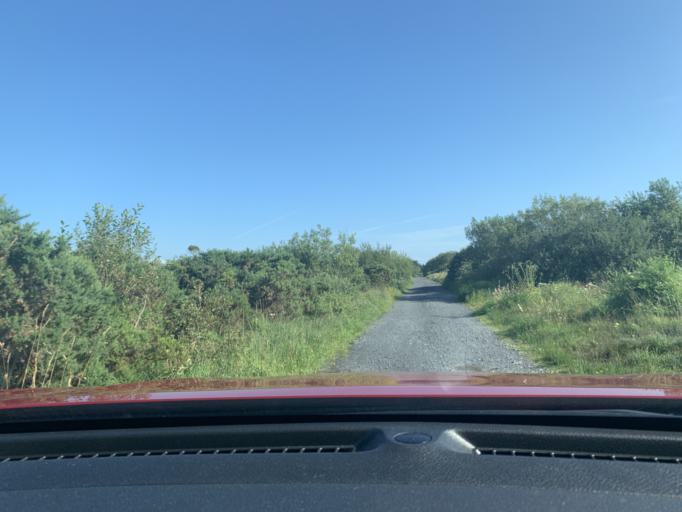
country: IE
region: Connaught
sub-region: Sligo
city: Tobercurry
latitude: 54.0662
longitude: -8.7931
